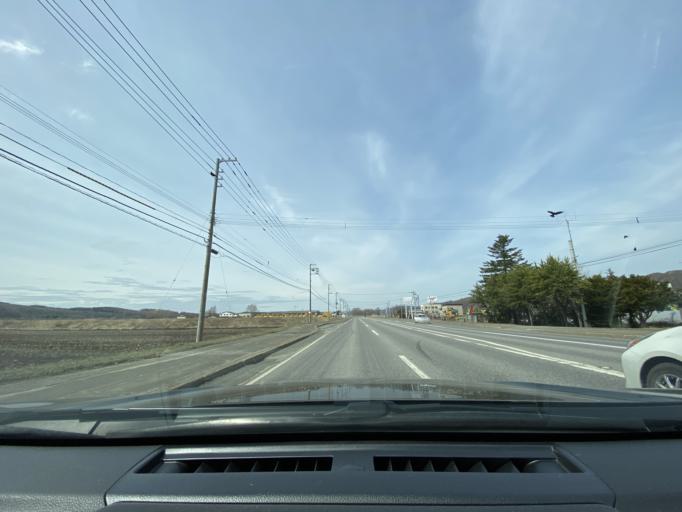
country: JP
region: Hokkaido
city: Kitami
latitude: 43.8021
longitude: 143.7937
